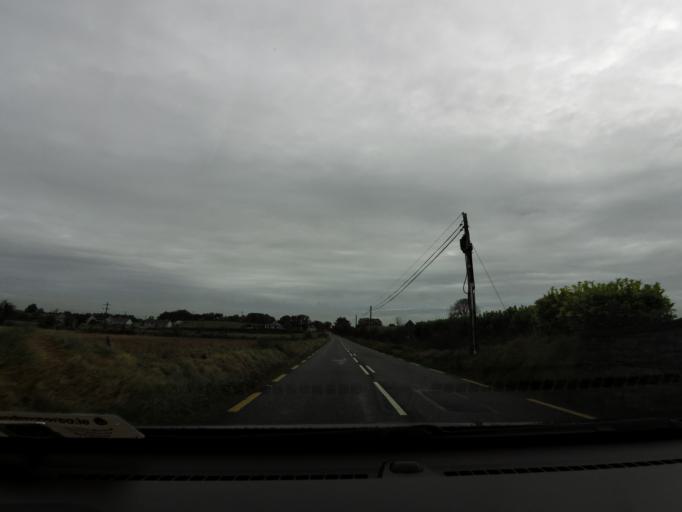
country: IE
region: Connaught
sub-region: County Galway
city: Tuam
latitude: 53.5927
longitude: -8.7722
